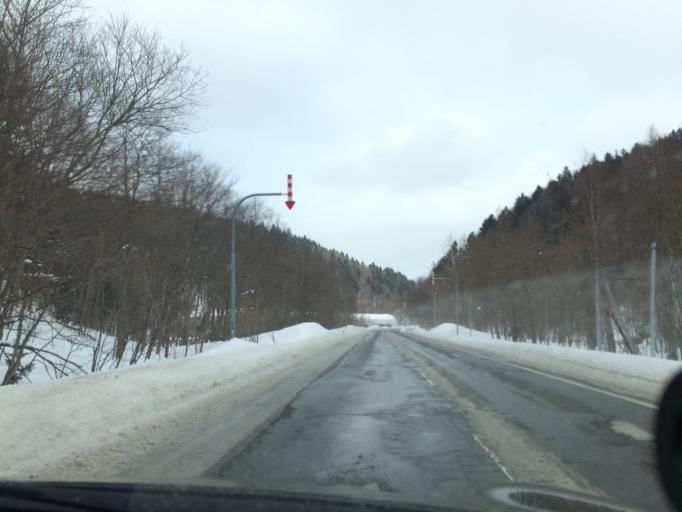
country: JP
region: Hokkaido
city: Shimo-furano
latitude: 43.0700
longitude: 142.6694
